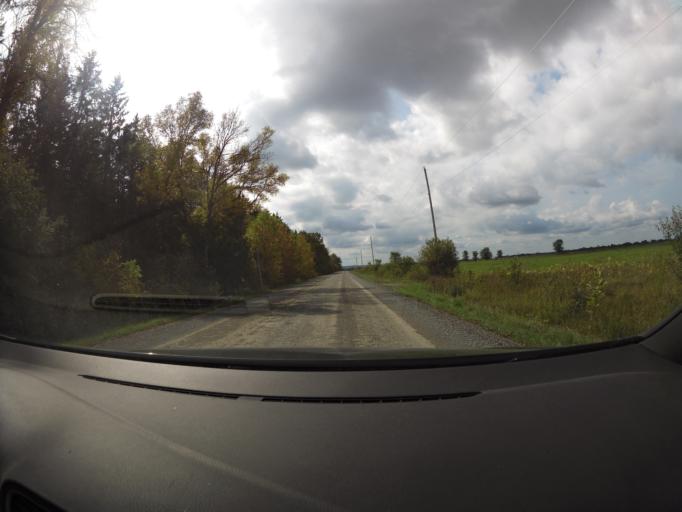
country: CA
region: Ontario
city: Arnprior
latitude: 45.4022
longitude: -76.2310
